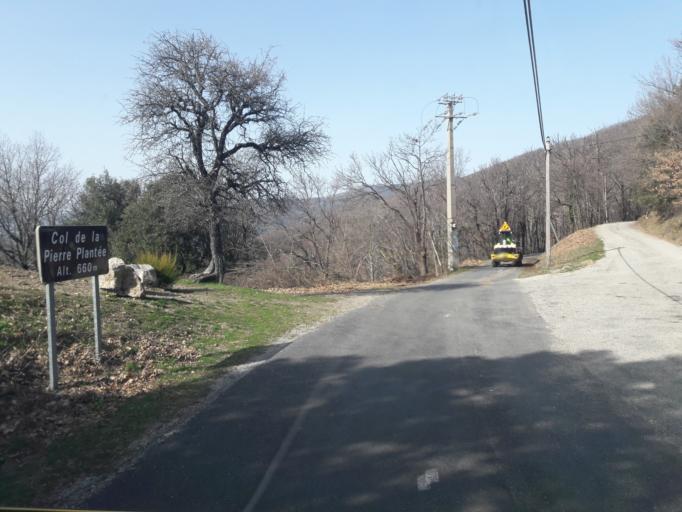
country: FR
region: Languedoc-Roussillon
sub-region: Departement du Gard
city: Sumene
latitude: 44.0118
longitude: 3.7792
